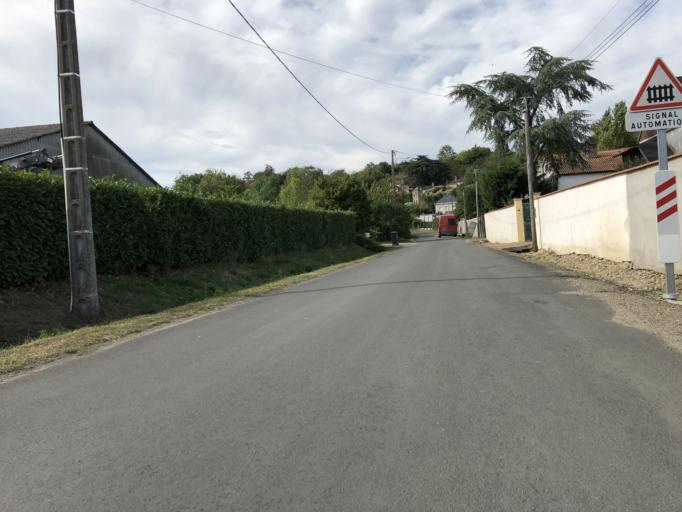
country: FR
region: Pays de la Loire
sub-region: Departement de la Sarthe
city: Chateau-du-Loir
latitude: 47.6811
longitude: 0.4269
